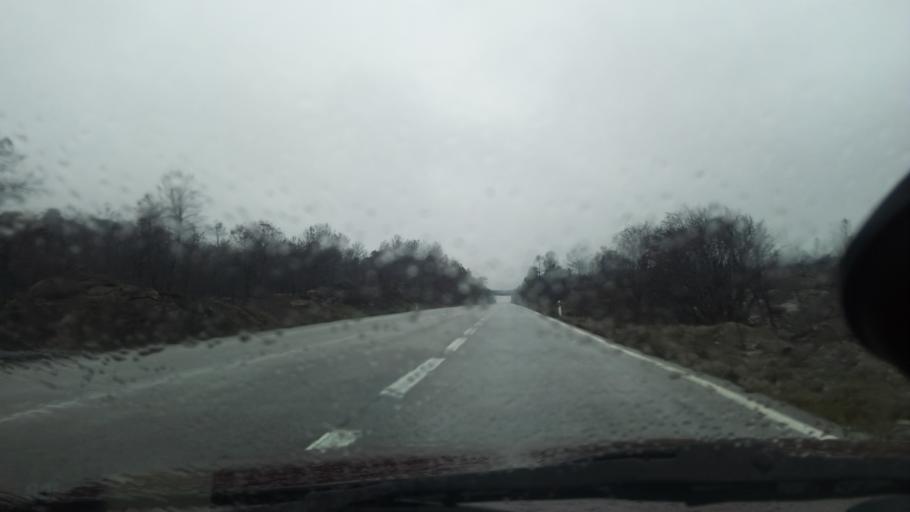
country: PT
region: Guarda
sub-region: Fornos de Algodres
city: Fornos de Algodres
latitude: 40.6147
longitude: -7.5997
